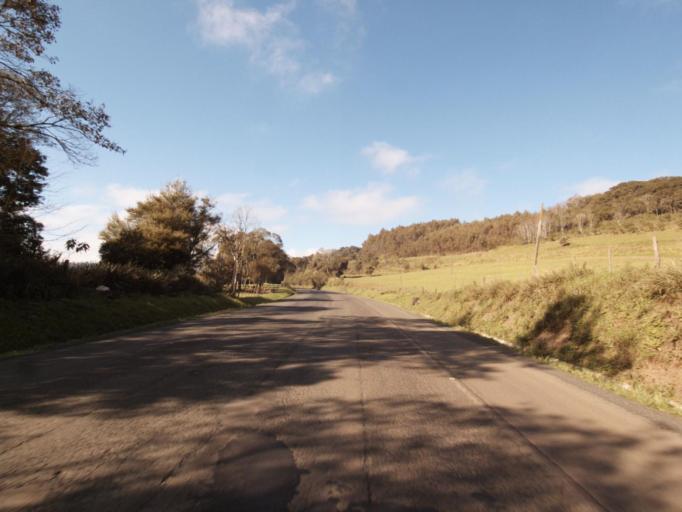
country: BR
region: Rio Grande do Sul
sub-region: Frederico Westphalen
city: Frederico Westphalen
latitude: -27.0556
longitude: -53.2281
